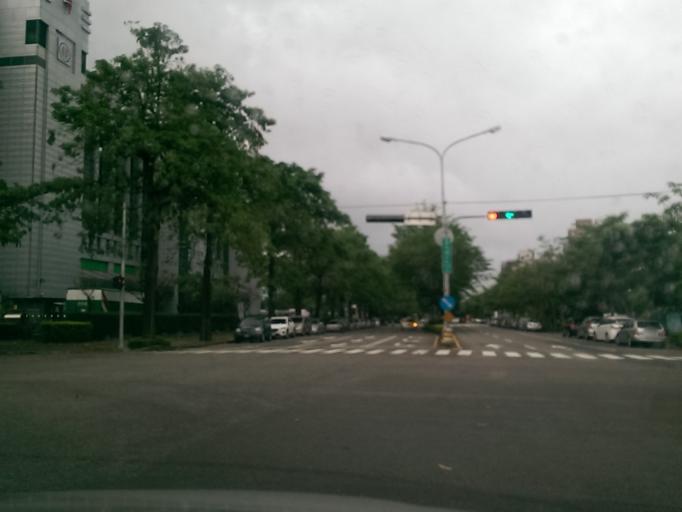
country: TW
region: Taiwan
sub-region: Taichung City
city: Taichung
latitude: 24.1470
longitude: 120.6407
